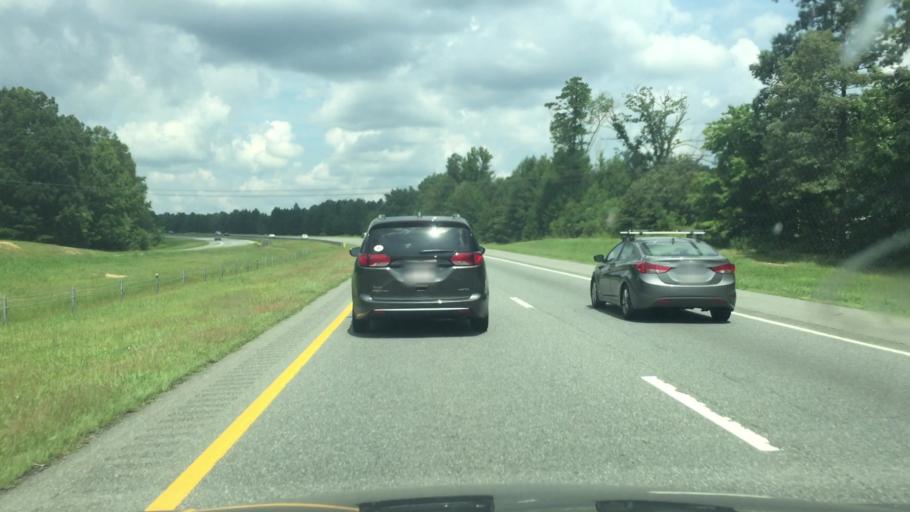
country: US
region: North Carolina
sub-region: Randolph County
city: Asheboro
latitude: 35.6101
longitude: -79.8189
